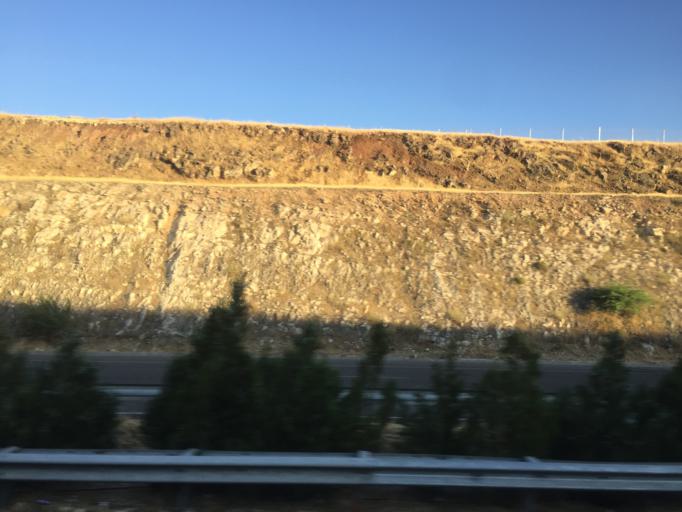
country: TR
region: Sanliurfa
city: Bogurtlen
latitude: 37.1012
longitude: 38.2021
